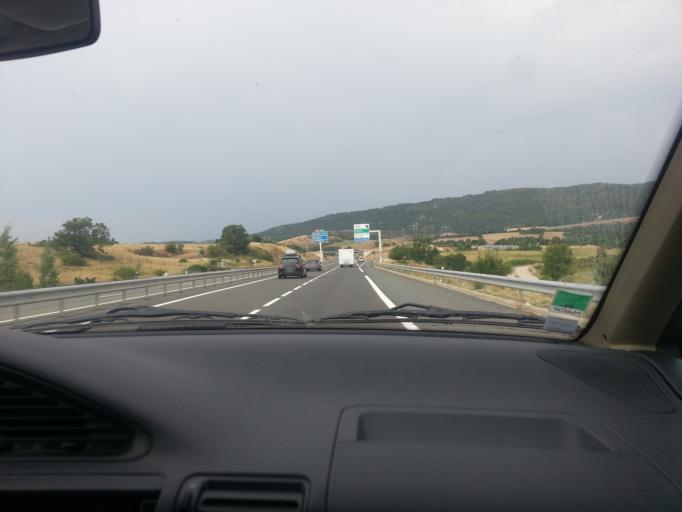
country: FR
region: Midi-Pyrenees
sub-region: Departement de l'Aveyron
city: Severac-le-Chateau
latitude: 44.3279
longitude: 3.0872
